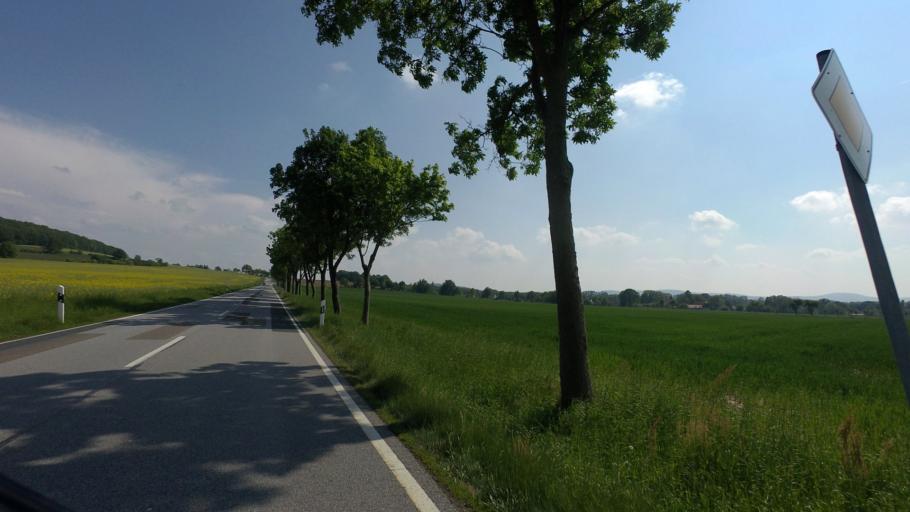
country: DE
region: Saxony
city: Weissenberg
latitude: 51.1839
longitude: 14.6436
